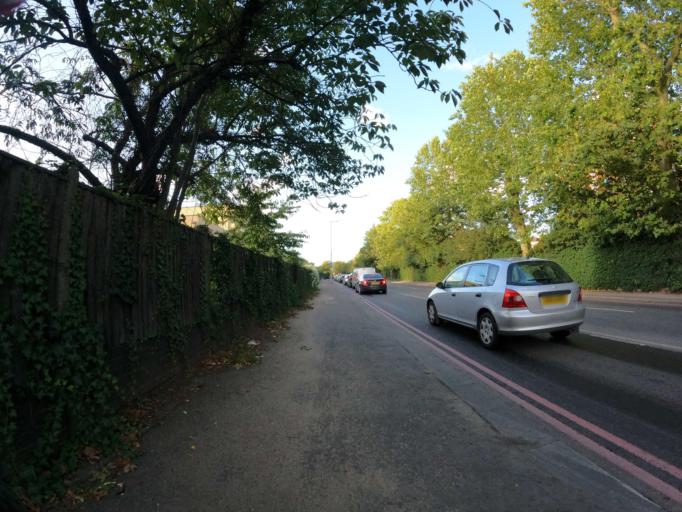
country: GB
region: England
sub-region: Greater London
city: Ealing Broadway
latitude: 51.5185
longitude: -0.2914
